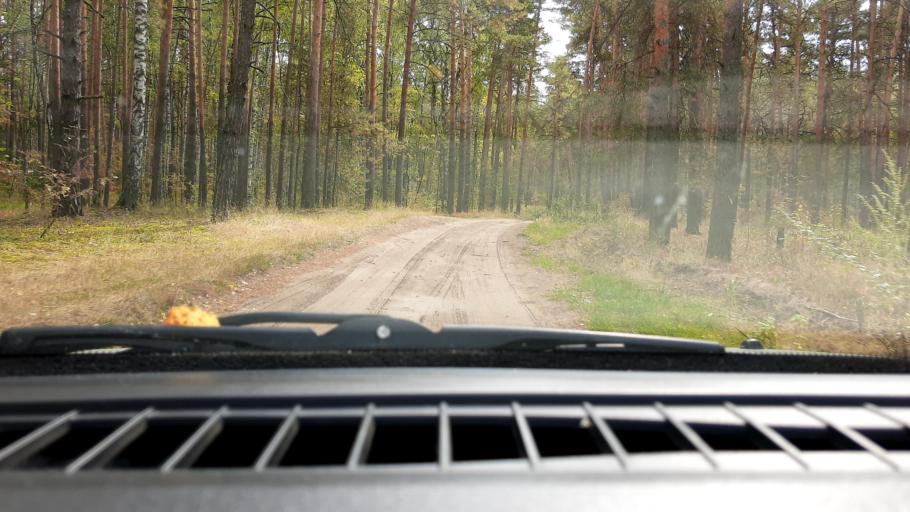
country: RU
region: Nizjnij Novgorod
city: Gorbatovka
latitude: 56.3233
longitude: 43.6915
